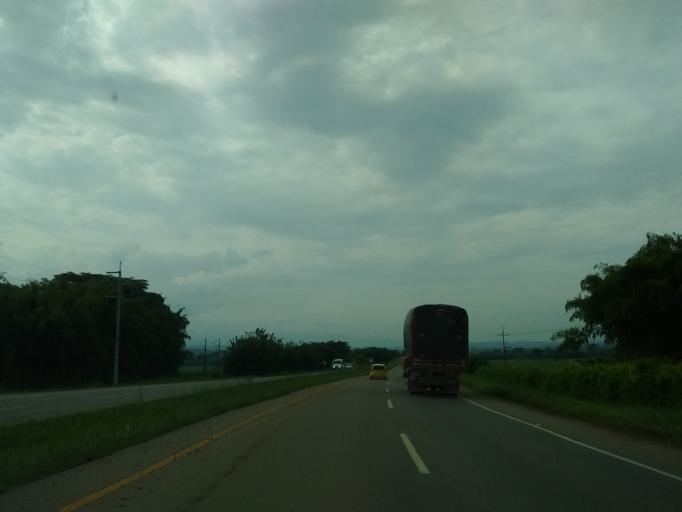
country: CO
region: Cauca
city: Santander de Quilichao
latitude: 3.0576
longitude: -76.4747
